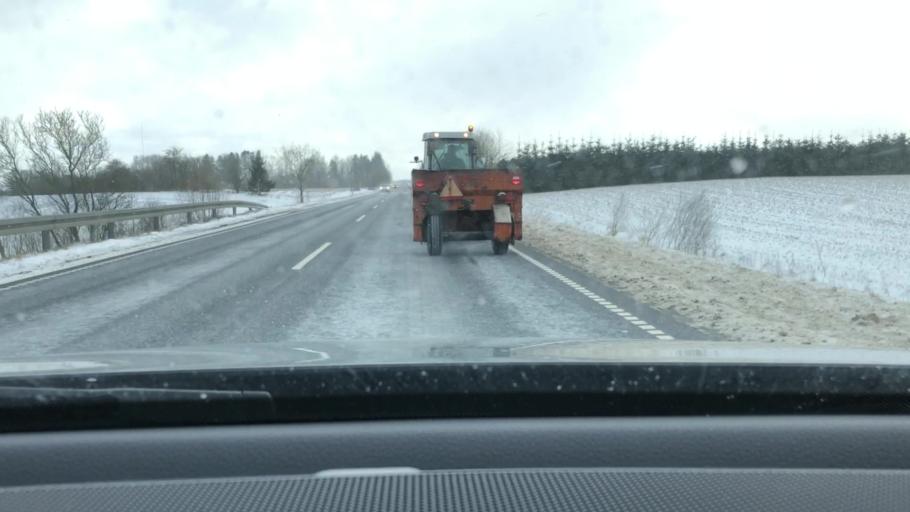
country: DK
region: Central Jutland
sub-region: Favrskov Kommune
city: Hammel
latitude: 56.1924
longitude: 9.8493
